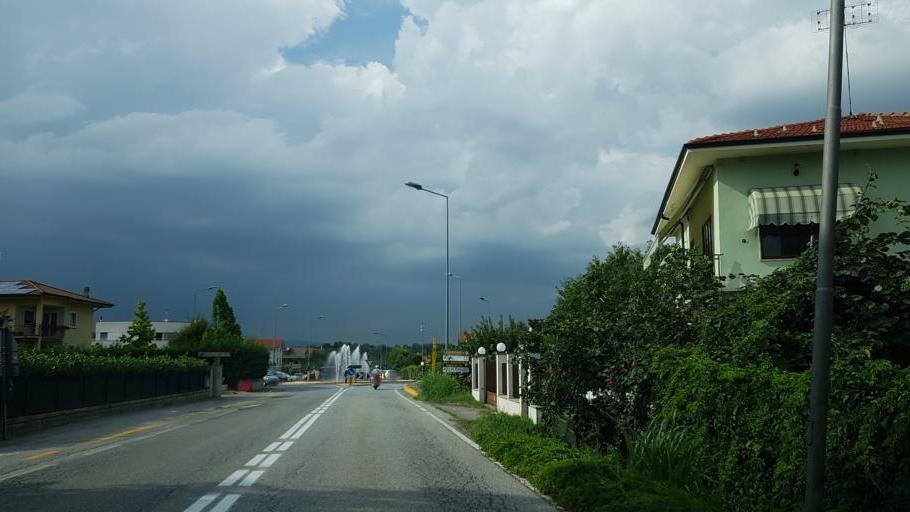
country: IT
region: Piedmont
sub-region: Provincia di Cuneo
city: Vignolo
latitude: 44.3601
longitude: 7.4766
